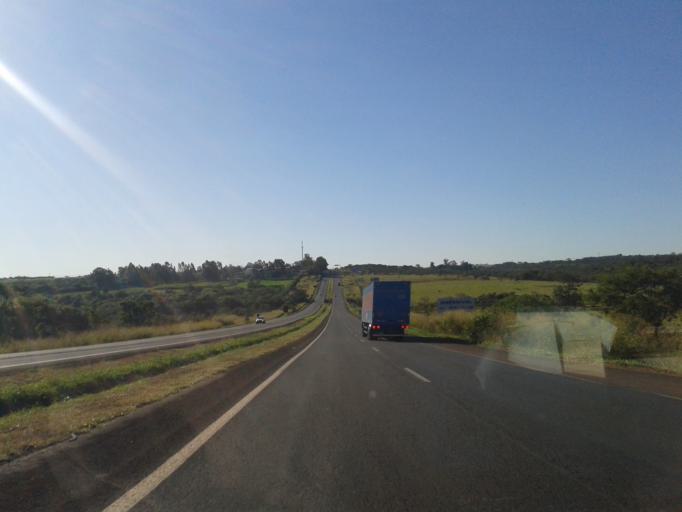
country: BR
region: Minas Gerais
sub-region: Uberlandia
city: Uberlandia
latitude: -18.9920
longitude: -48.2111
